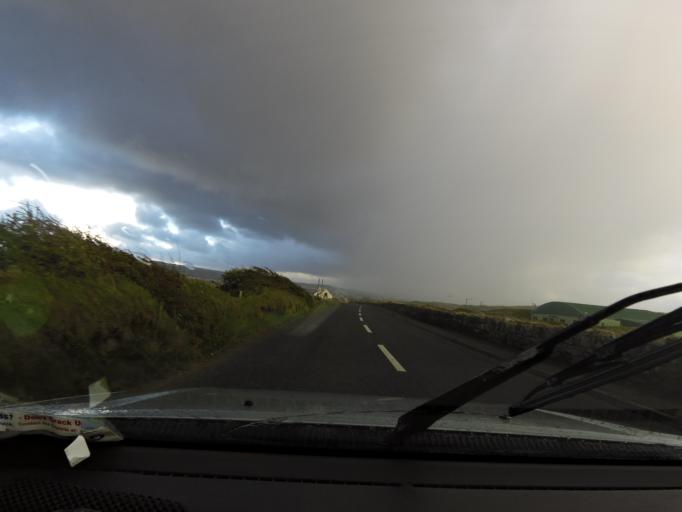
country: IE
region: Munster
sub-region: An Clar
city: Kilrush
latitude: 52.9454
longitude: -9.3511
